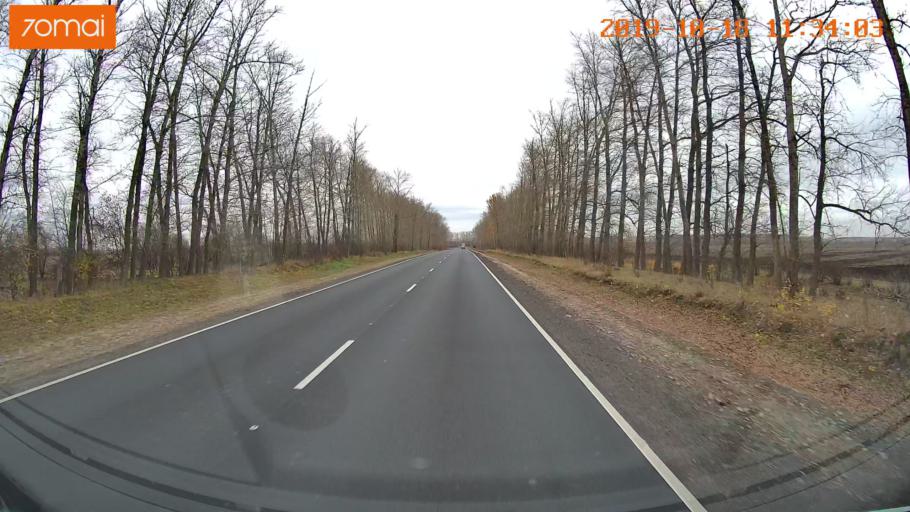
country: RU
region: Rjazan
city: Oktyabr'skiy
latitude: 54.1375
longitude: 38.7557
